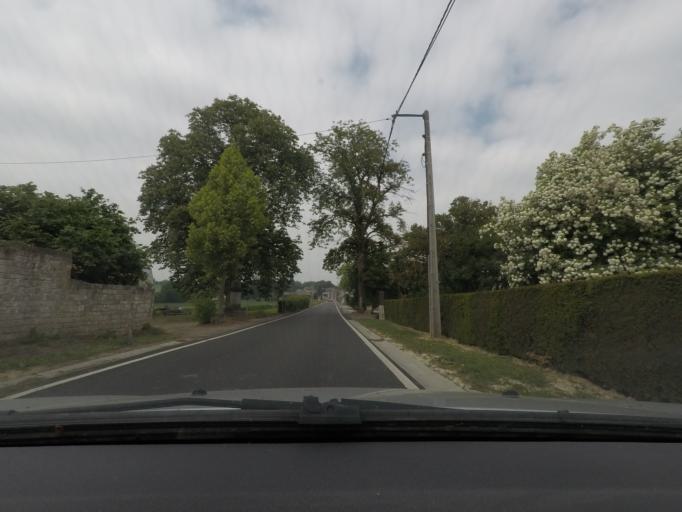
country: BE
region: Wallonia
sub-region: Province de Namur
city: Noville-les-Bois
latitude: 50.4930
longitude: 5.0072
